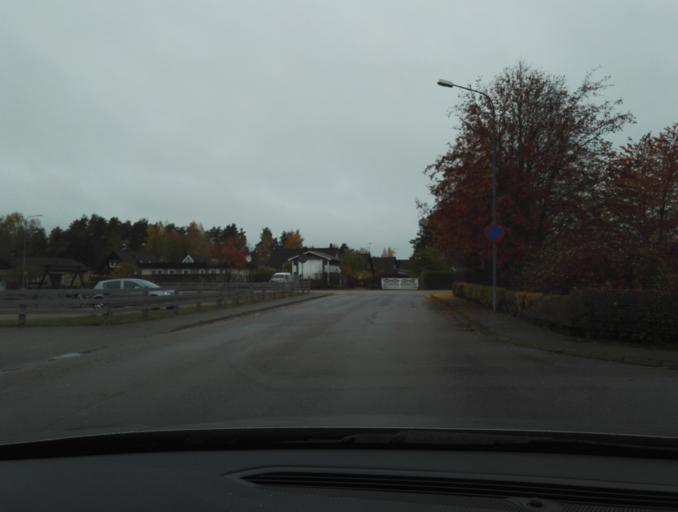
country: SE
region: Kronoberg
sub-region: Vaxjo Kommun
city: Rottne
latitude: 57.0263
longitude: 14.8960
